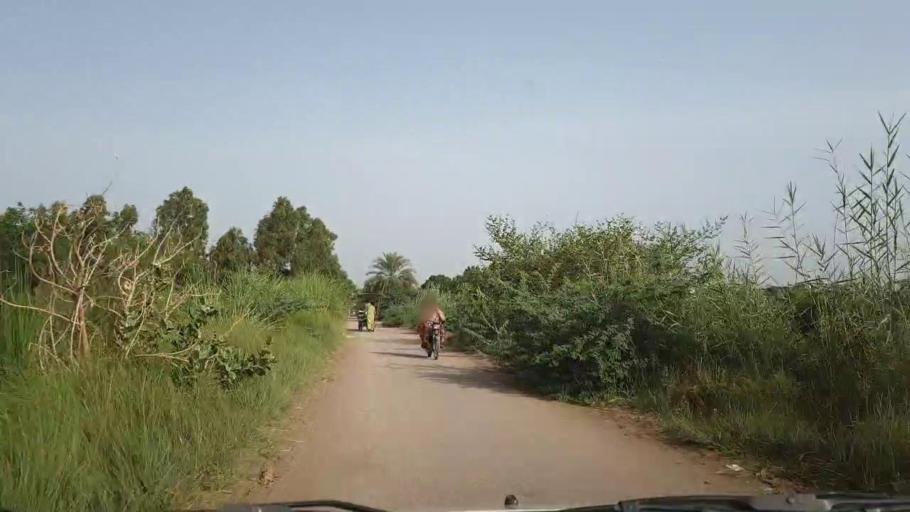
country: PK
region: Sindh
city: Nawabshah
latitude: 26.2315
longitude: 68.4088
